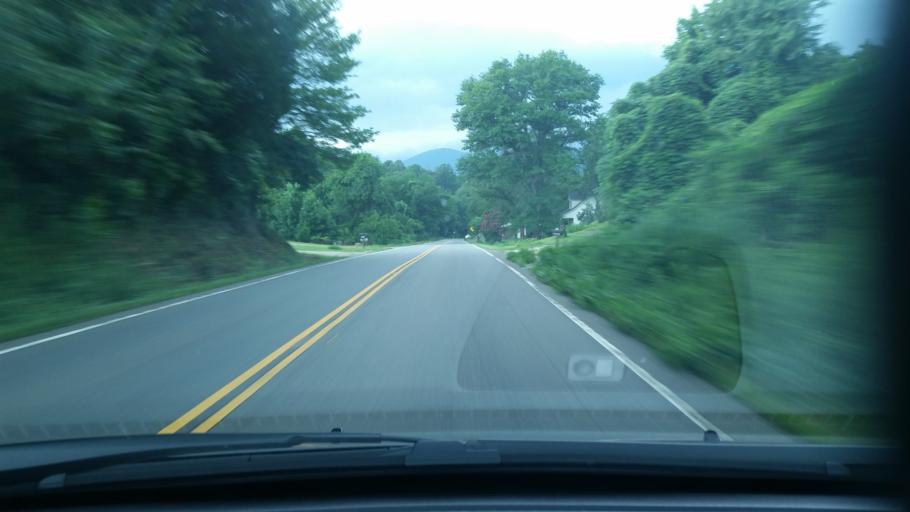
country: US
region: Virginia
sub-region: Nelson County
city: Nellysford
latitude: 37.8637
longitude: -78.8159
